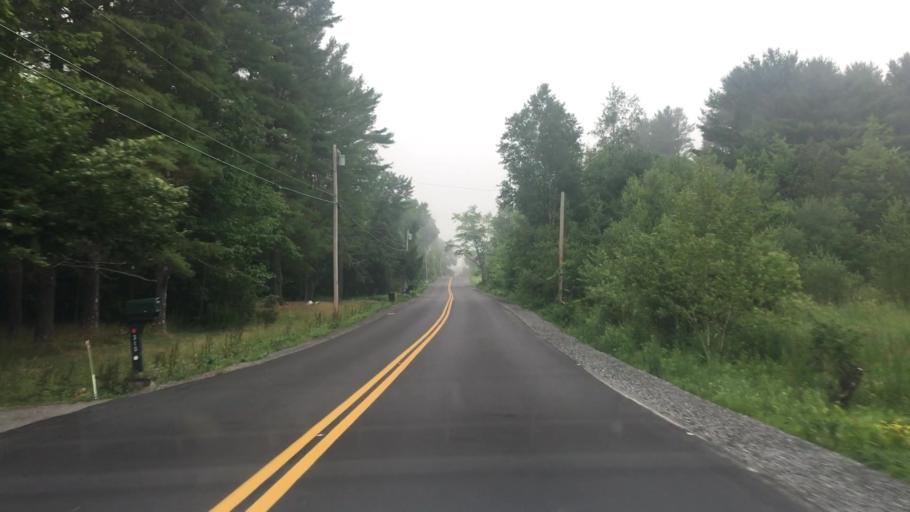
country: US
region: Maine
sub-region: Kennebec County
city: Oakland
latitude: 44.5138
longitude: -69.7127
